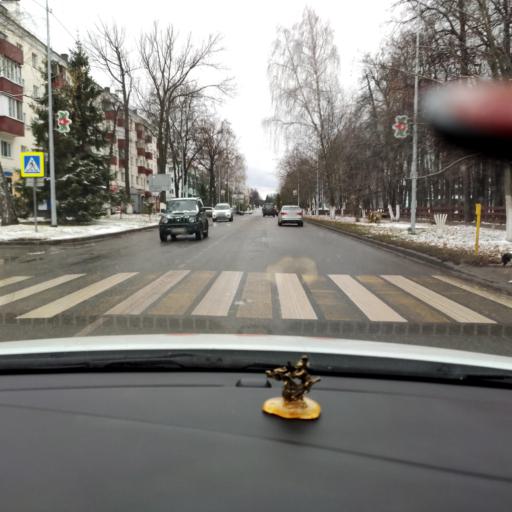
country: RU
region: Tatarstan
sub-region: Zelenodol'skiy Rayon
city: Zelenodolsk
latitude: 55.8462
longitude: 48.5077
